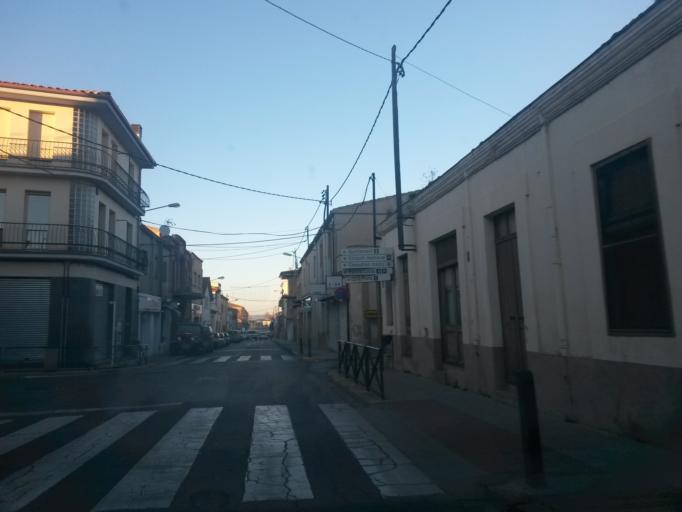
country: ES
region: Catalonia
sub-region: Provincia de Girona
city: Pals
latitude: 41.9695
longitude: 3.1486
